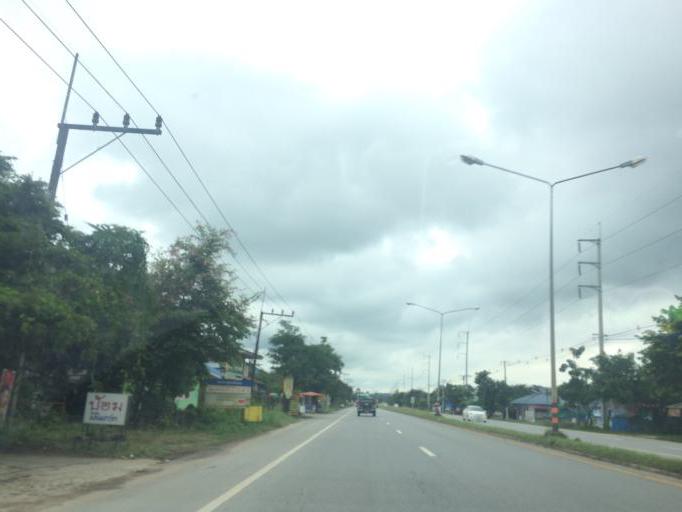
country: TH
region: Chiang Rai
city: Mae Chan
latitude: 20.0768
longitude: 99.8754
